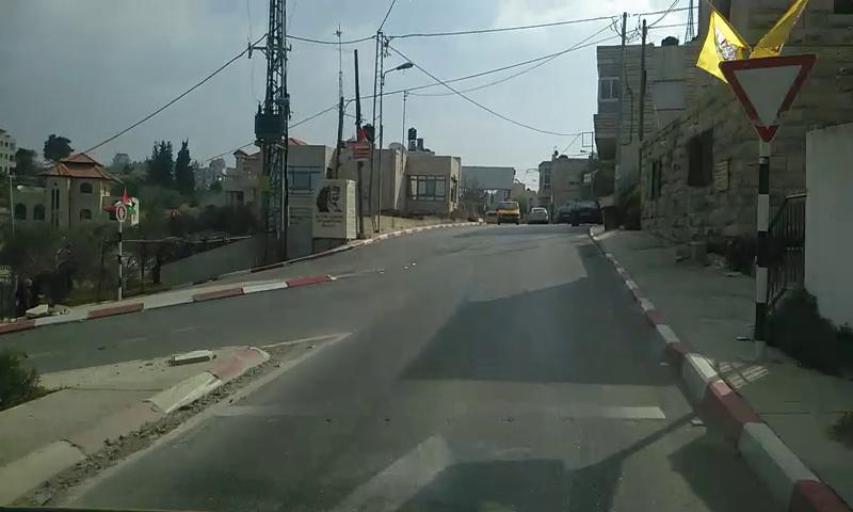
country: PS
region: West Bank
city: Dura al Qar`
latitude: 31.9580
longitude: 35.2250
